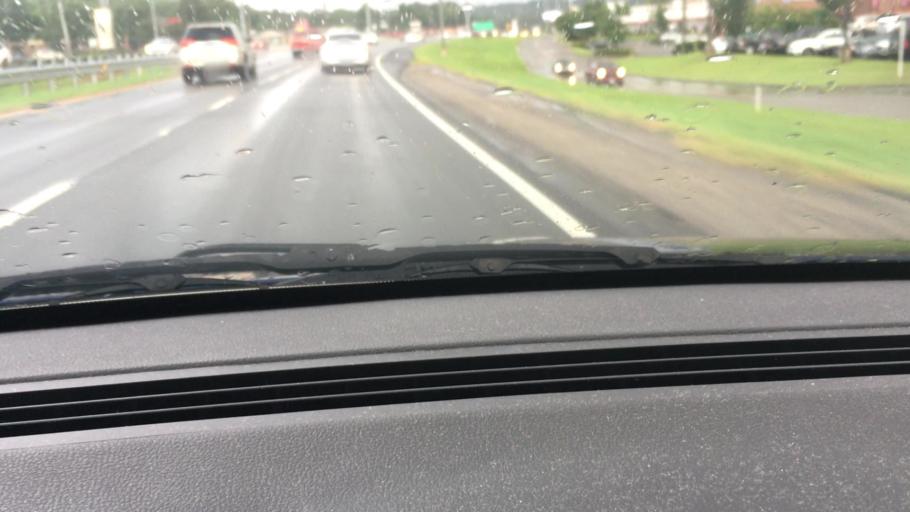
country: US
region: Alabama
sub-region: Tuscaloosa County
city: Tuscaloosa
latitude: 33.2327
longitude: -87.5385
